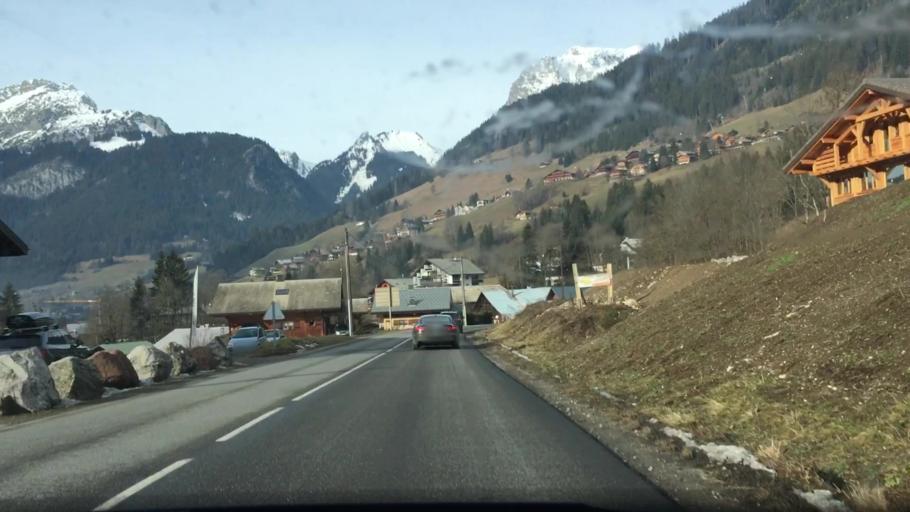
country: FR
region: Rhone-Alpes
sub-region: Departement de la Haute-Savoie
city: Chatel
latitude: 46.2865
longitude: 6.8091
